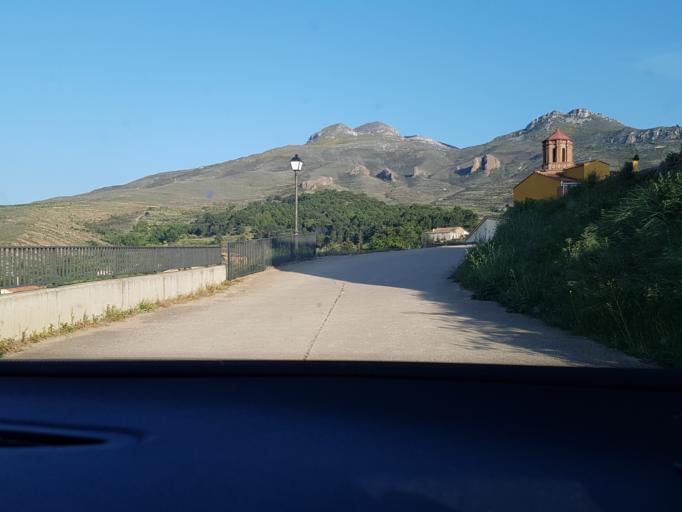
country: ES
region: La Rioja
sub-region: Provincia de La Rioja
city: Prejano
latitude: 42.1880
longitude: -2.1795
